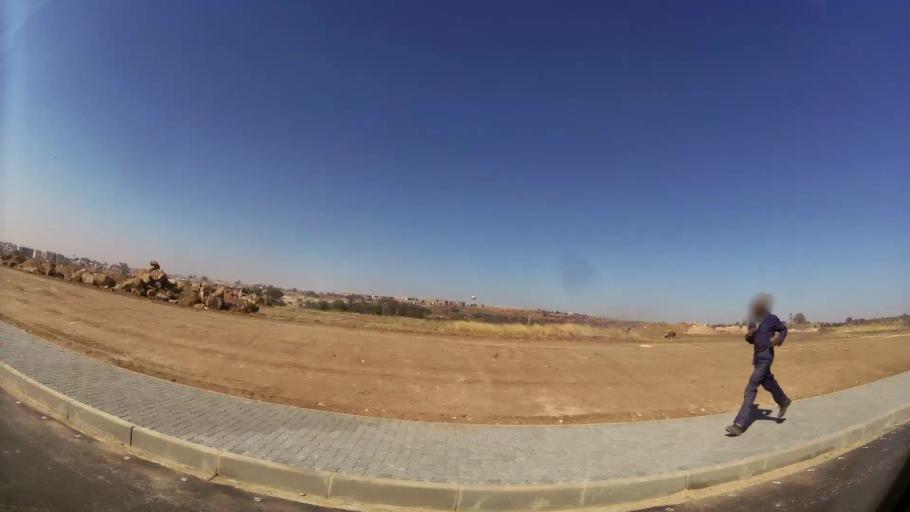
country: ZA
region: Gauteng
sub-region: City of Johannesburg Metropolitan Municipality
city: Johannesburg
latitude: -26.2441
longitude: 28.0766
